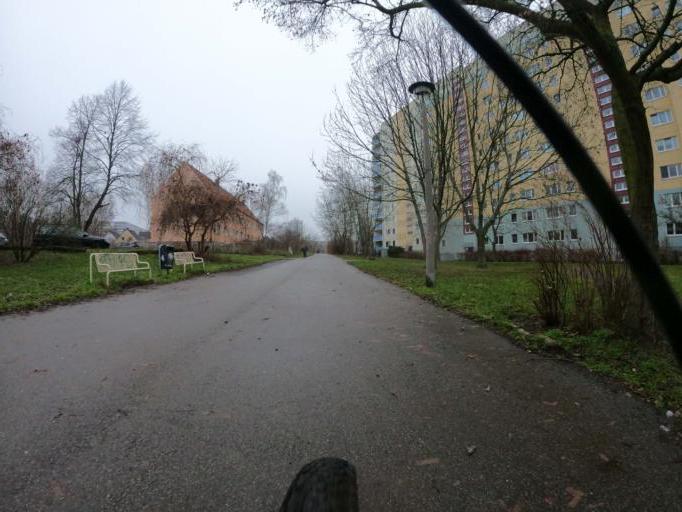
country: DE
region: Berlin
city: Marzahn
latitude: 52.5374
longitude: 13.5632
